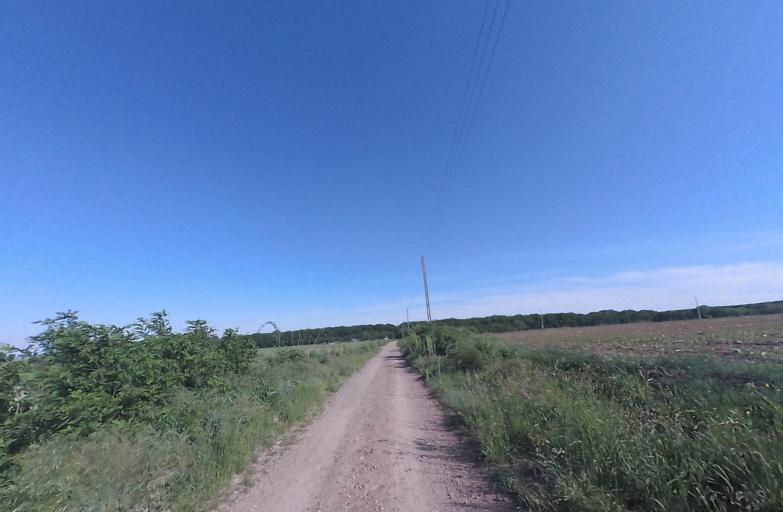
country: RO
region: Neamt
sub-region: Comuna Dulcesti
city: Dulcesti
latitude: 46.9992
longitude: 26.7797
